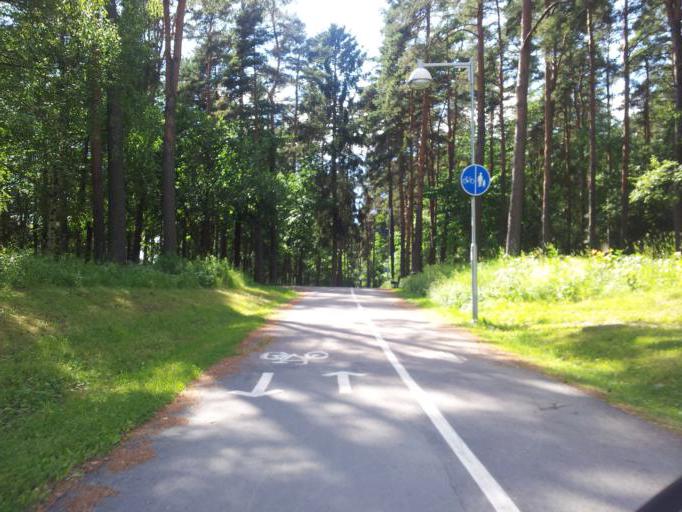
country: SE
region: Uppsala
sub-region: Uppsala Kommun
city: Uppsala
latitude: 59.8792
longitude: 17.6551
